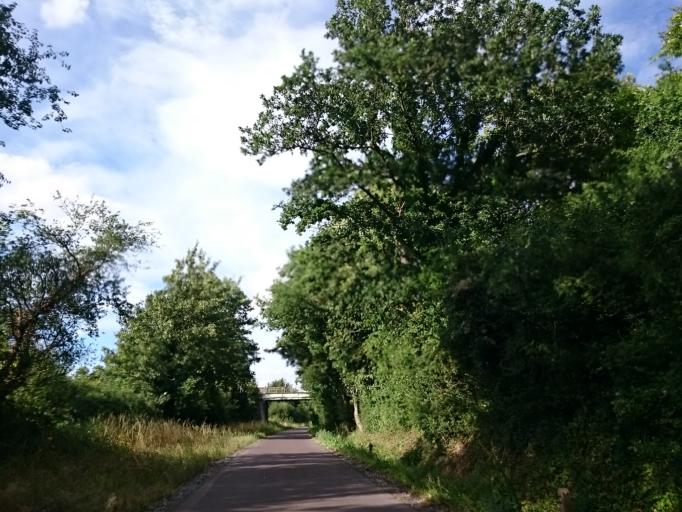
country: FR
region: Lower Normandy
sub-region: Departement du Calvados
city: Saint-Andre-sur-Orne
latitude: 49.1315
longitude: -0.4015
